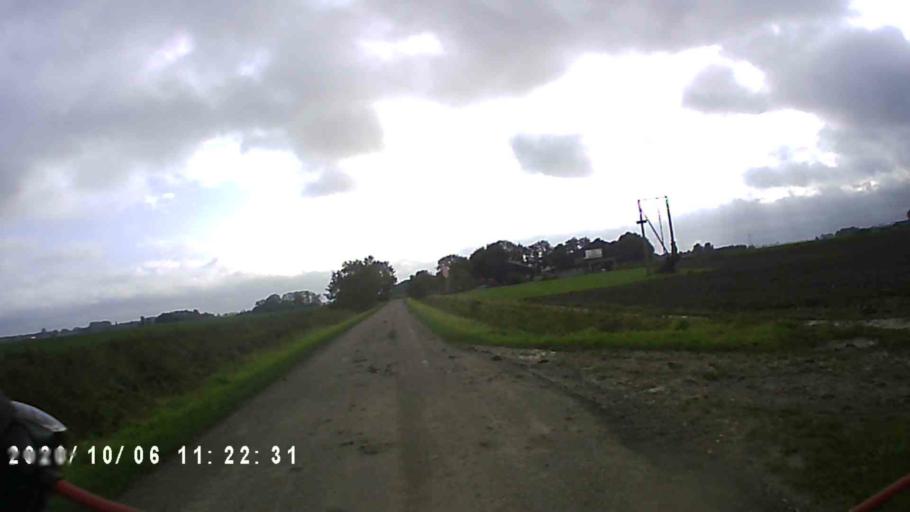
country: NL
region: Groningen
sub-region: Gemeente Zuidhorn
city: Oldehove
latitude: 53.3460
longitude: 6.4122
